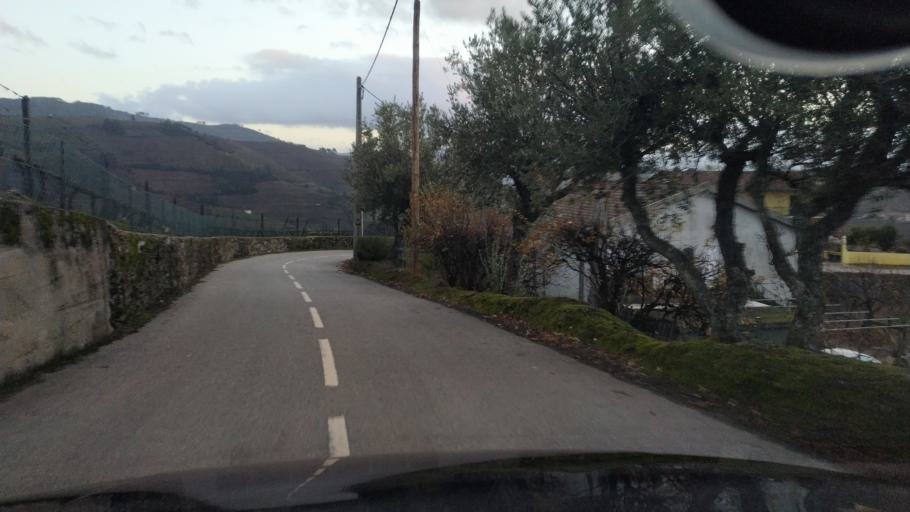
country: PT
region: Vila Real
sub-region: Santa Marta de Penaguiao
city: Santa Marta de Penaguiao
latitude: 41.2394
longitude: -7.7724
